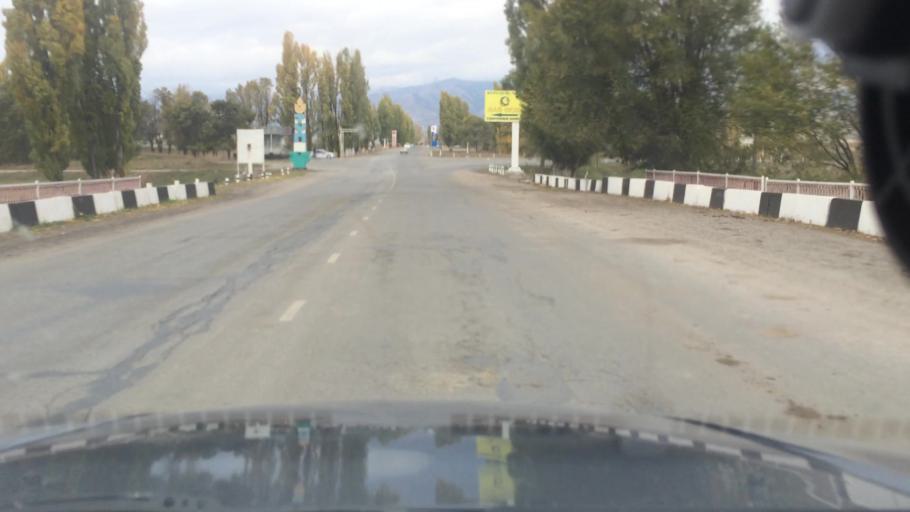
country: KG
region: Ysyk-Koel
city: Tyup
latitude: 42.7381
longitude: 78.3468
